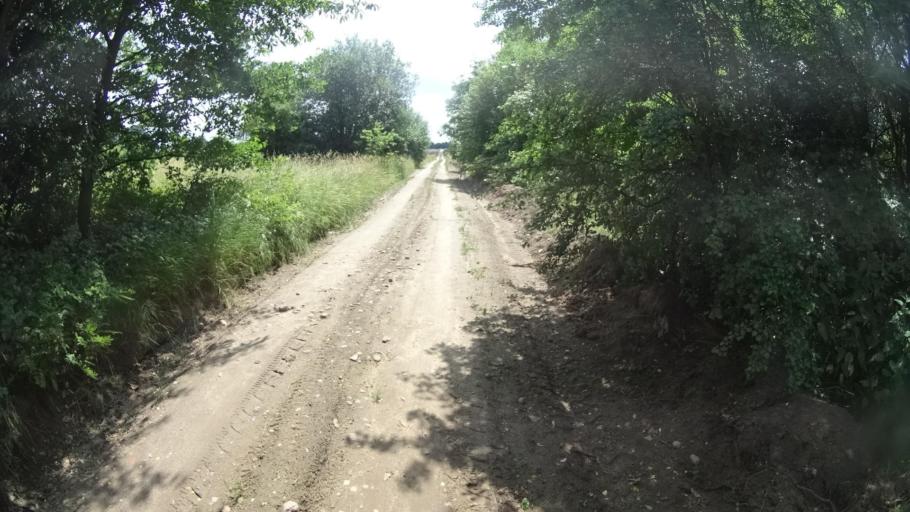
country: PL
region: Masovian Voivodeship
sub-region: Powiat grojecki
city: Goszczyn
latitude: 51.7016
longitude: 20.8254
